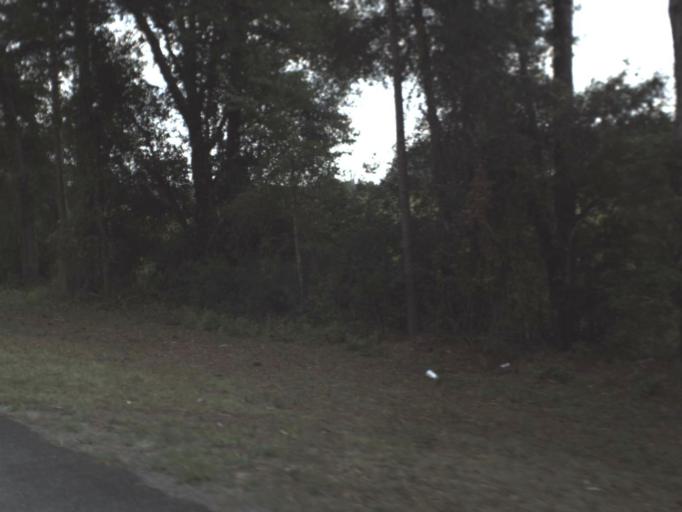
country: US
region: Florida
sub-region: Madison County
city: Madison
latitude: 30.4866
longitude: -83.2233
